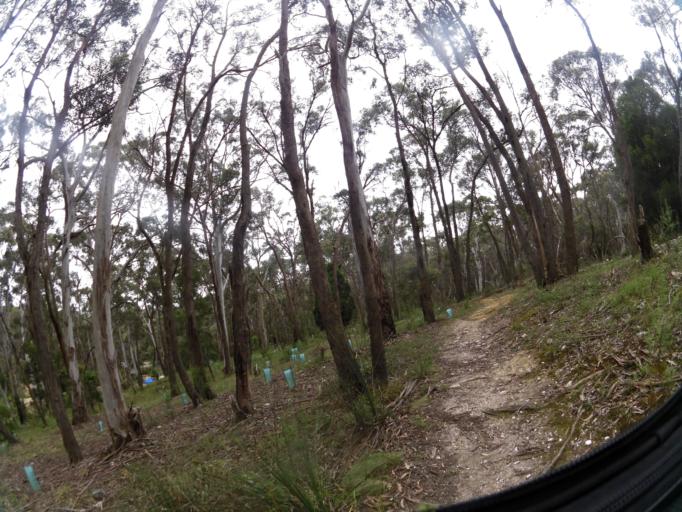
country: AU
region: Victoria
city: Brown Hill
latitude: -37.4638
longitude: 143.9047
